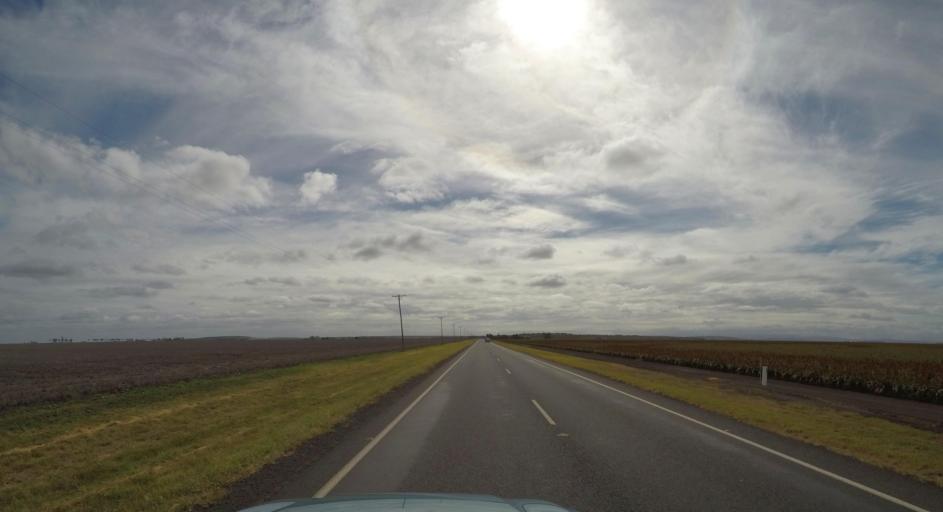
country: AU
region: Queensland
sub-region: Western Downs
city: Dalby
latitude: -27.1329
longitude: 151.3024
